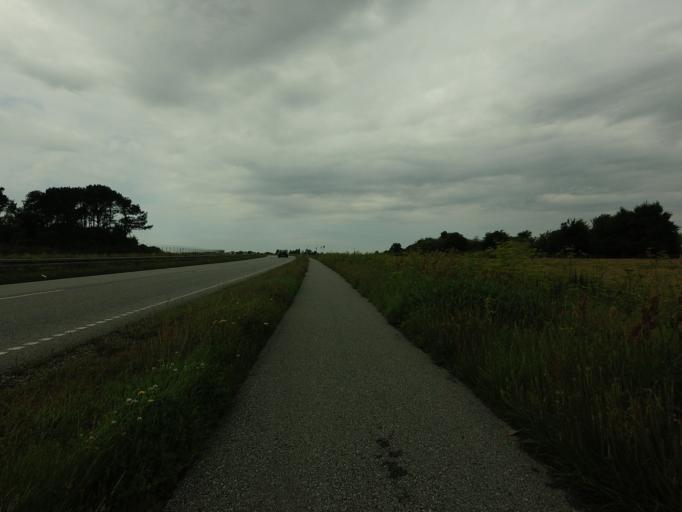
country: DK
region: North Denmark
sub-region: Alborg Kommune
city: Vadum
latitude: 57.1067
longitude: 9.8783
